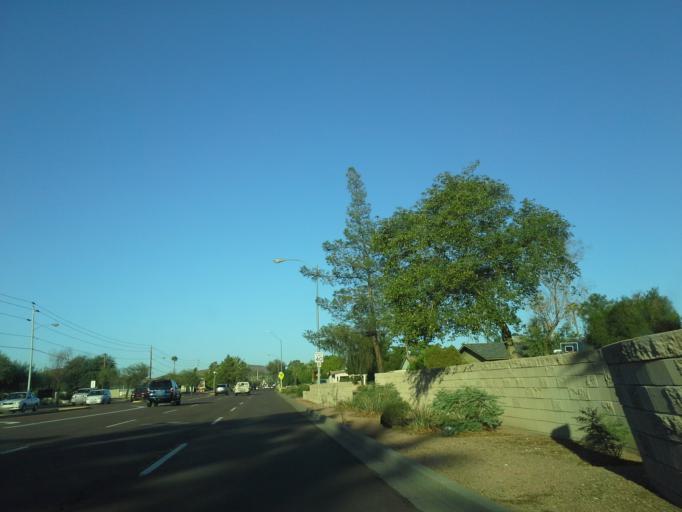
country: US
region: Arizona
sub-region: Maricopa County
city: Paradise Valley
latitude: 33.5969
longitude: -112.0265
